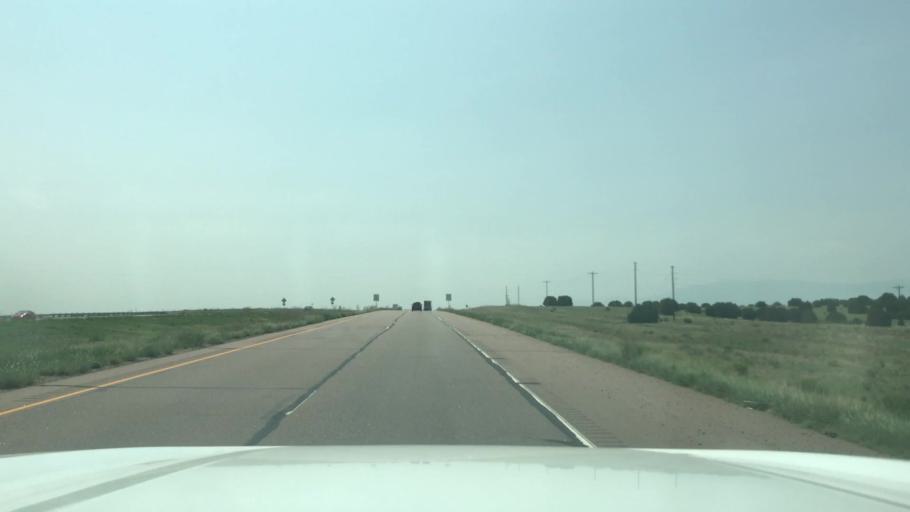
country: US
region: Colorado
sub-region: Pueblo County
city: Pueblo
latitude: 38.1136
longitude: -104.6743
